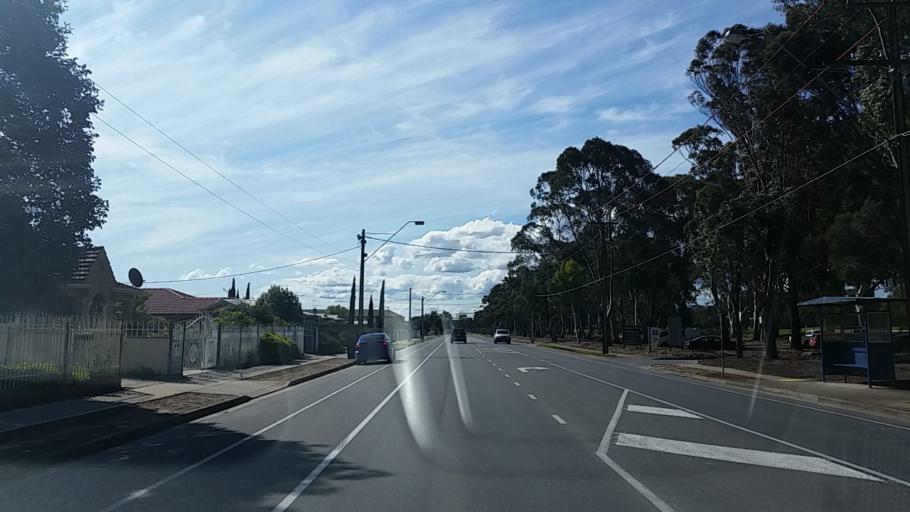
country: AU
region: South Australia
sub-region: Charles Sturt
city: Woodville North
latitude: -34.8652
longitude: 138.5656
